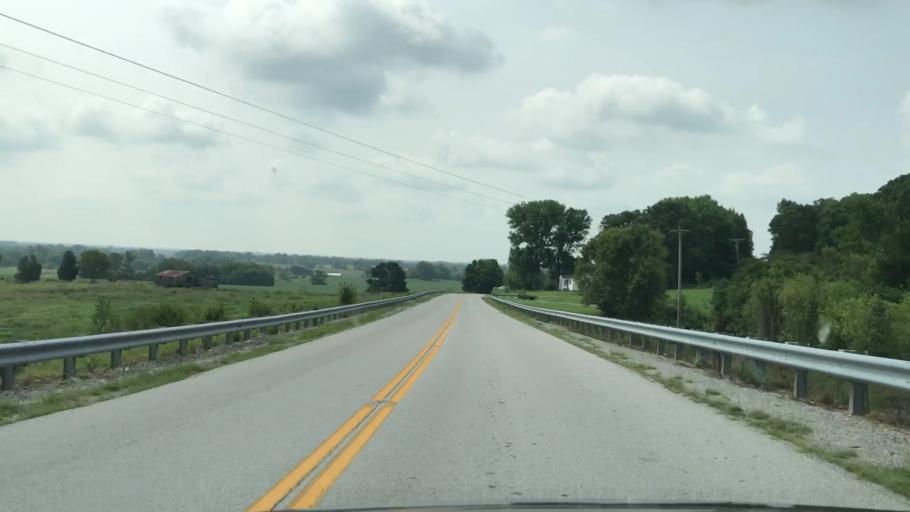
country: US
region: Kentucky
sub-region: Edmonson County
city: Brownsville
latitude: 37.1020
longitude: -86.1469
